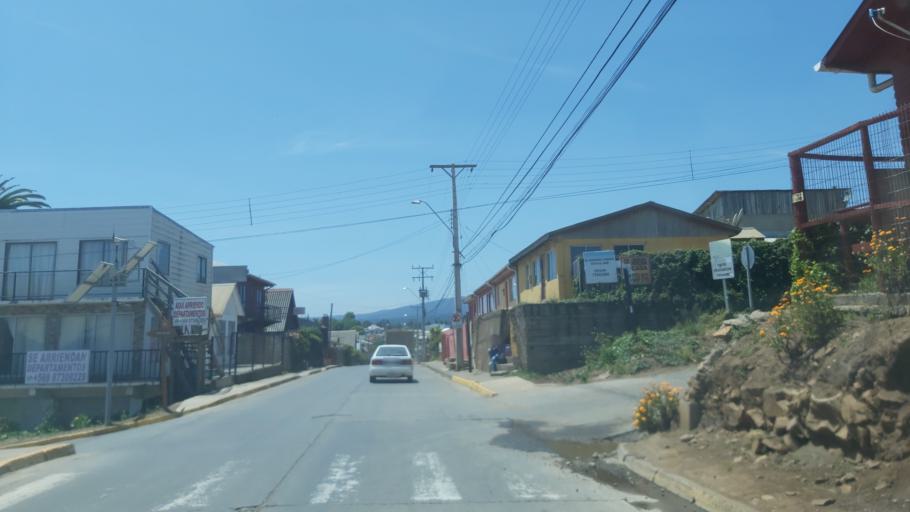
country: CL
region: Maule
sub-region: Provincia de Cauquenes
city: Cauquenes
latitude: -35.8150
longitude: -72.5749
